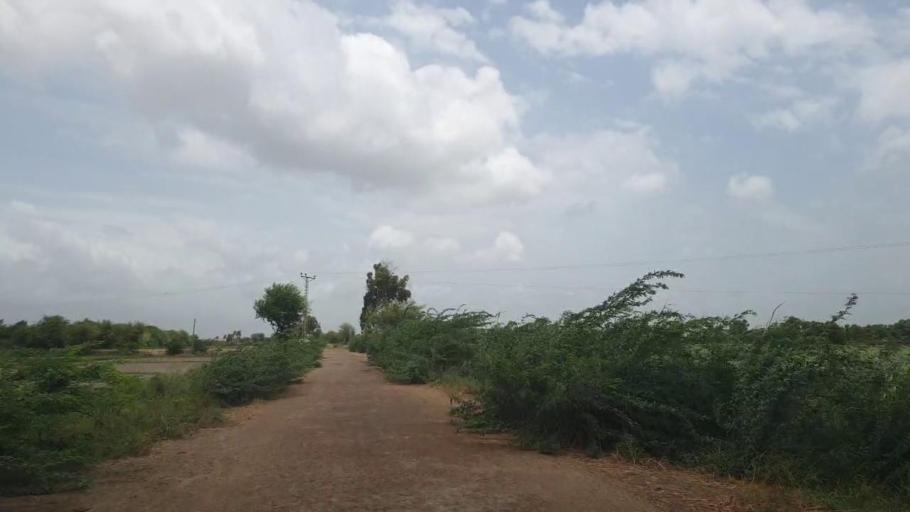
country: PK
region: Sindh
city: Badin
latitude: 24.6656
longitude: 68.8921
